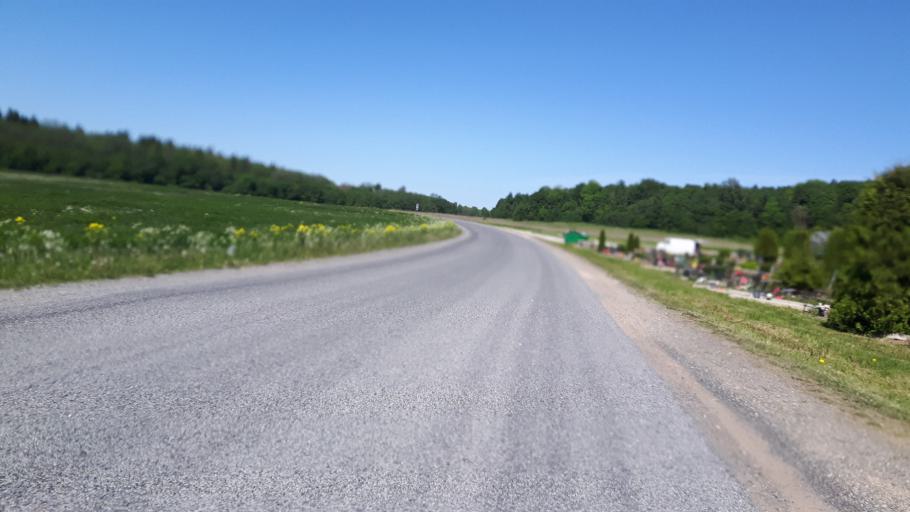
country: EE
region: Ida-Virumaa
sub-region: Sillamaee linn
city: Sillamae
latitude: 59.3731
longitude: 27.8428
